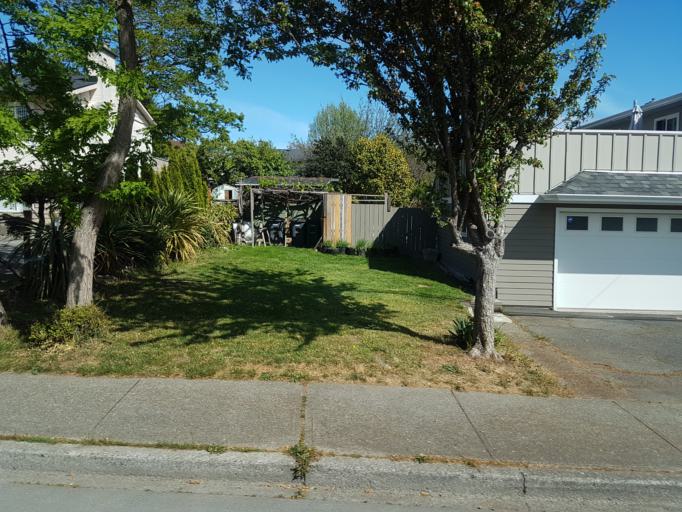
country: CA
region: British Columbia
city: Oak Bay
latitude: 48.4822
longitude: -123.3222
